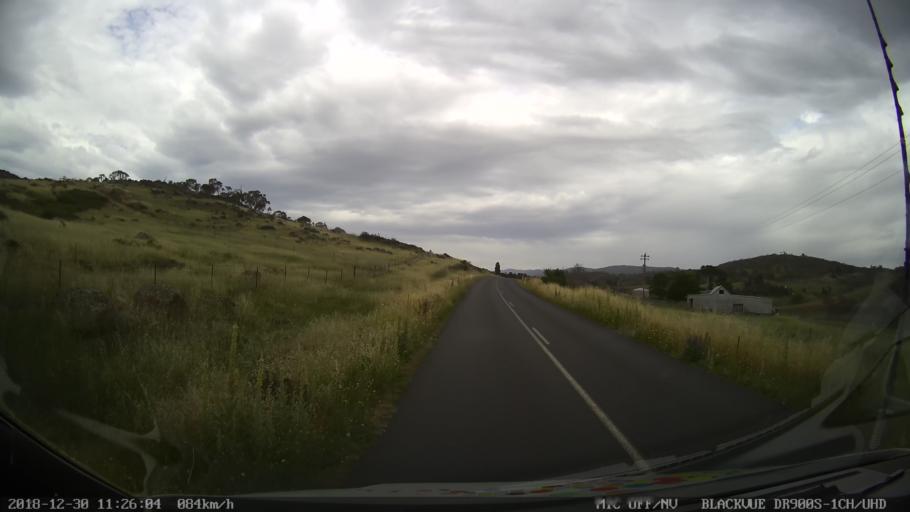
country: AU
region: New South Wales
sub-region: Snowy River
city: Jindabyne
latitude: -36.4687
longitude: 148.6391
